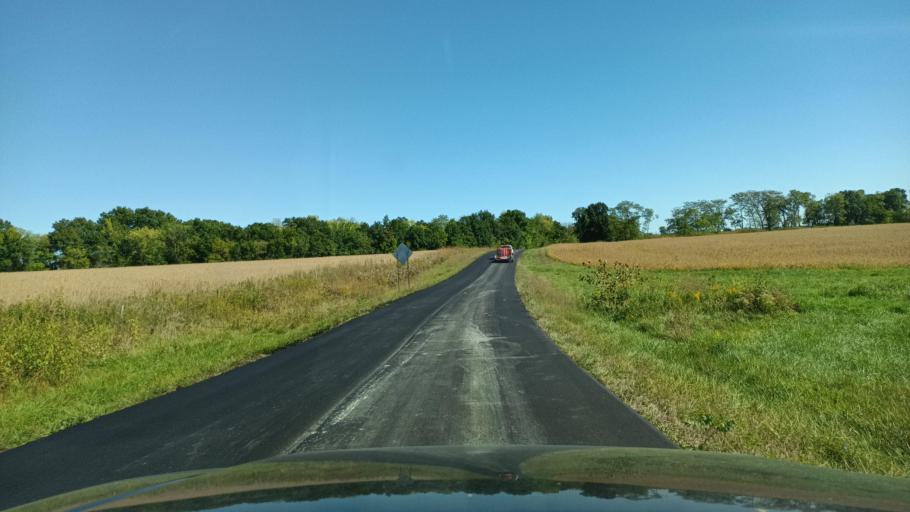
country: US
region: Missouri
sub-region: Macon County
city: La Plata
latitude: 39.9266
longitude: -92.5392
